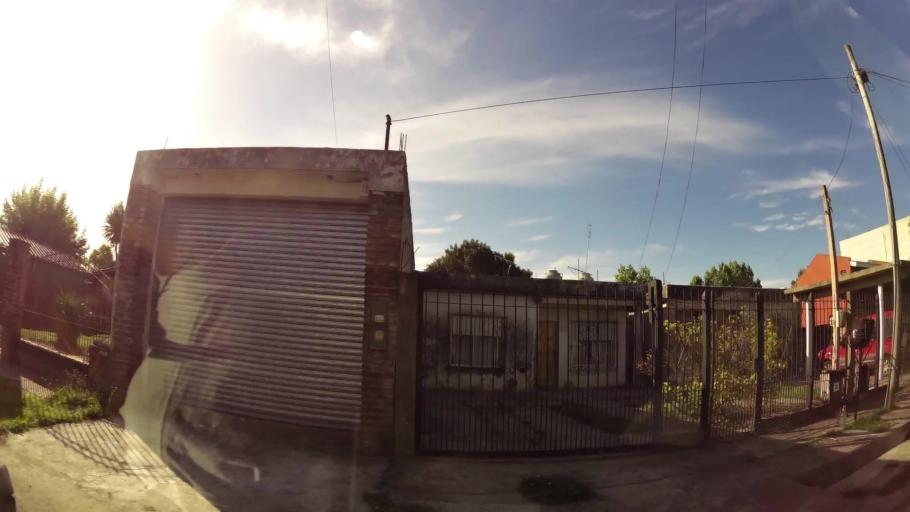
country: AR
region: Buenos Aires
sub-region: Partido de Quilmes
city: Quilmes
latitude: -34.7829
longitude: -58.2333
